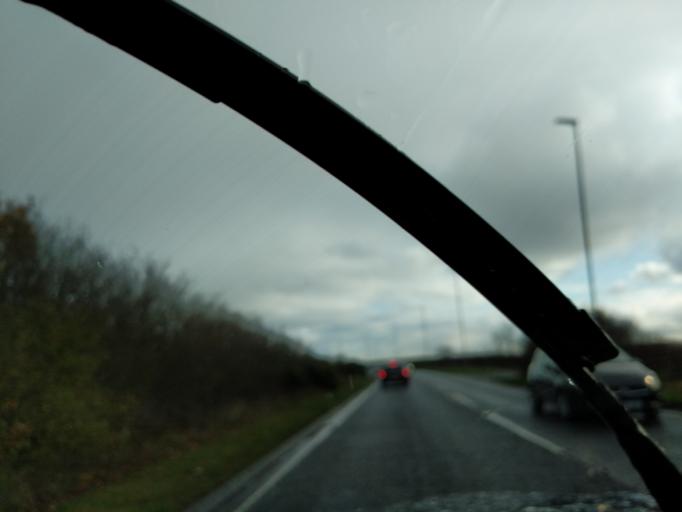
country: GB
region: England
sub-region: Northumberland
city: Seaton Delaval
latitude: 55.1024
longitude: -1.5336
